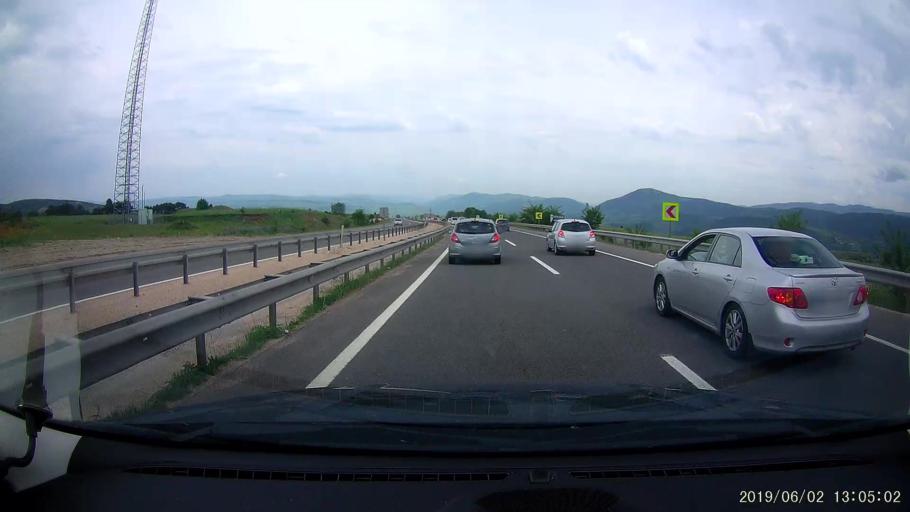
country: TR
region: Karabuk
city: Gozyeri
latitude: 40.8592
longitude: 32.5347
